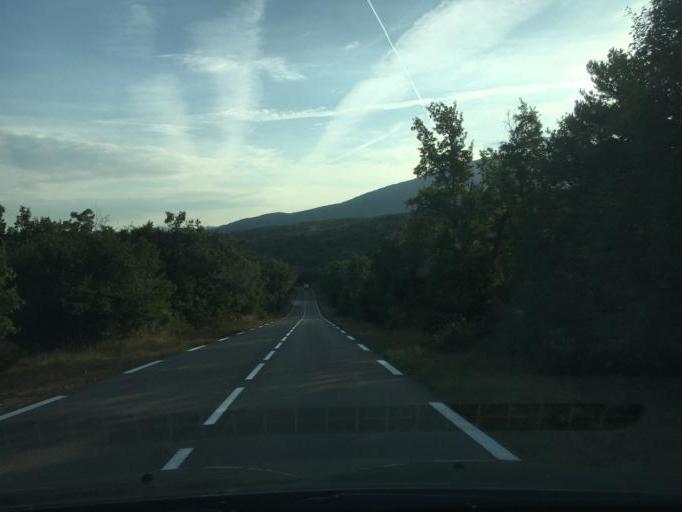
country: FR
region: Provence-Alpes-Cote d'Azur
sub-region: Departement du Var
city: Aups
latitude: 43.7343
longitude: 6.2202
